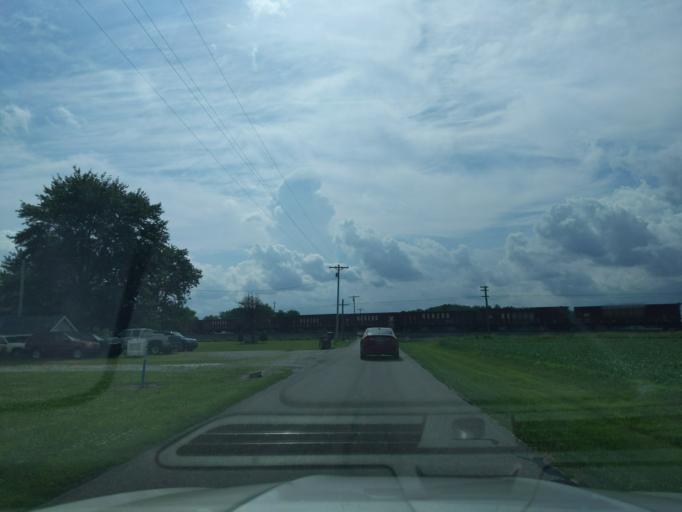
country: US
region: Indiana
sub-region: Ripley County
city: Osgood
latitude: 39.1183
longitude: -85.3020
